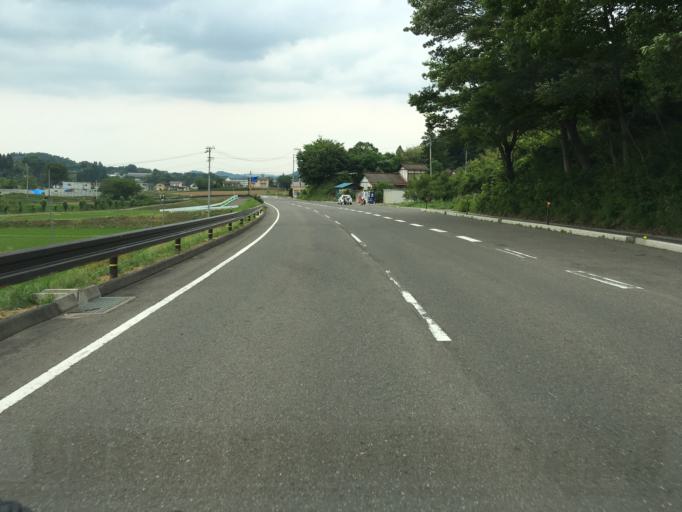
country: JP
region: Fukushima
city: Nihommatsu
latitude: 37.6480
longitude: 140.5349
